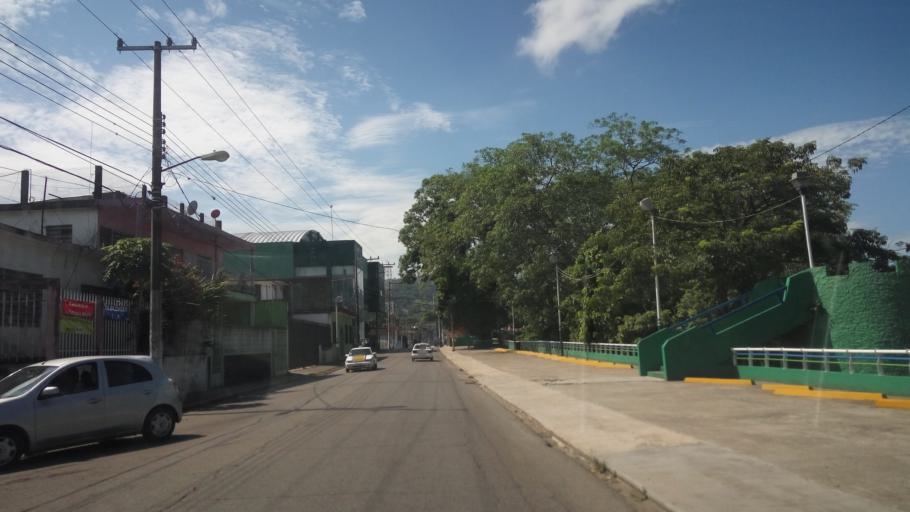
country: MX
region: Tabasco
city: Teapa
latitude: 17.5571
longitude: -92.9506
